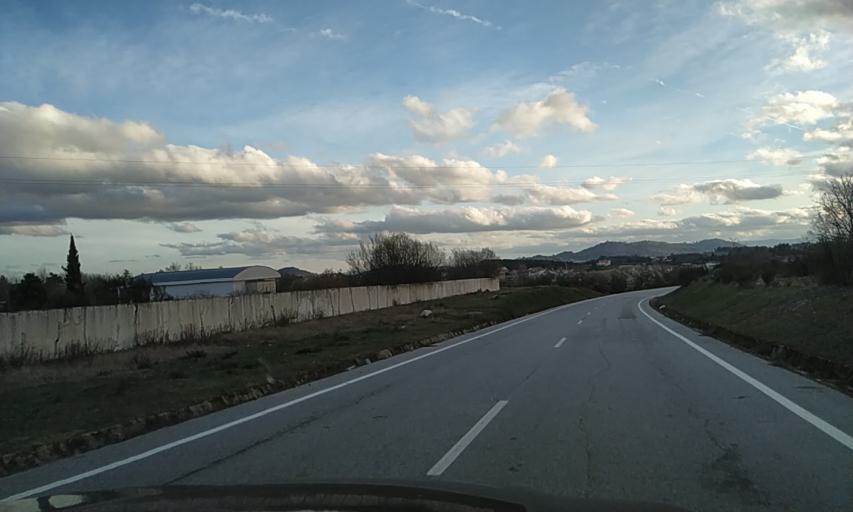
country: PT
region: Braganca
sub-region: Carrazeda de Ansiaes
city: Carrazeda de Anciaes
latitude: 41.2420
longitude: -7.3191
